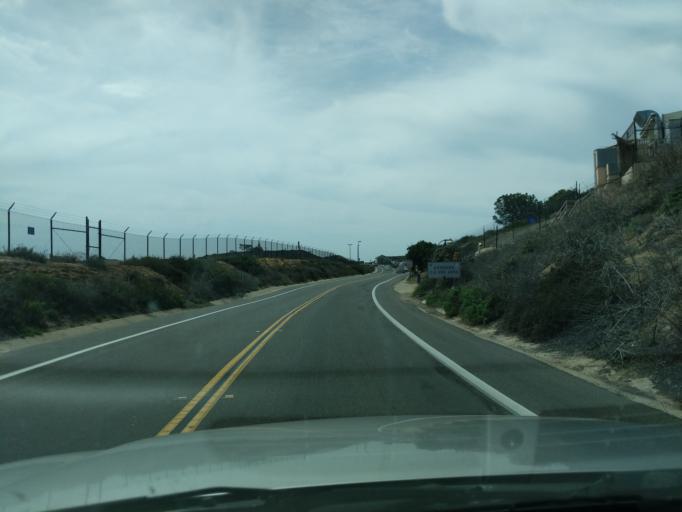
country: US
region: California
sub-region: San Diego County
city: Coronado
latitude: 32.6792
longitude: -117.2435
